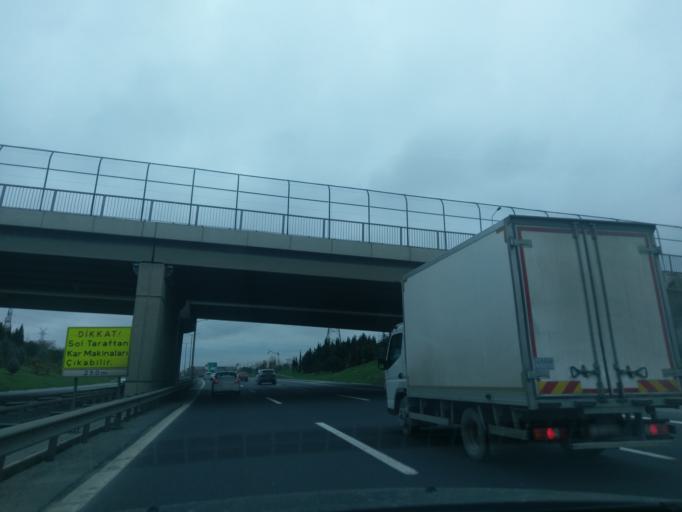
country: TR
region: Istanbul
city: Esenyurt
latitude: 41.0568
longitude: 28.6608
